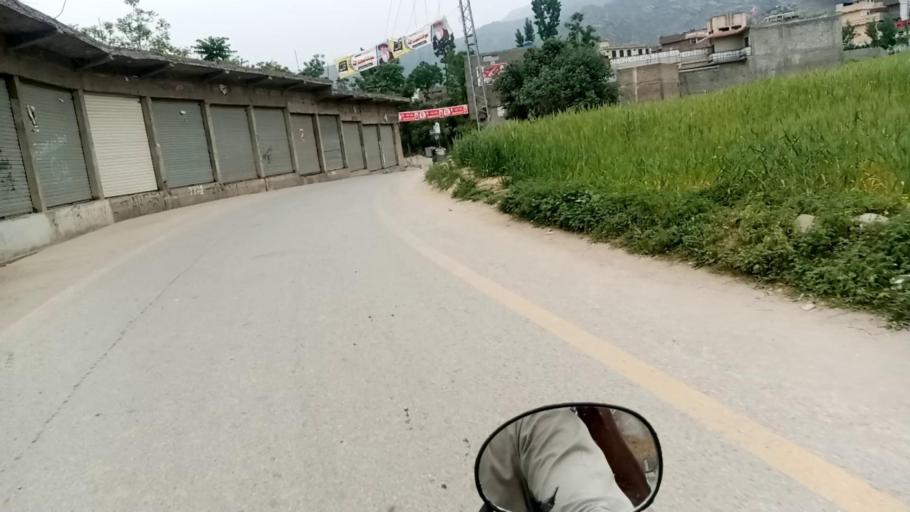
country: PK
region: Khyber Pakhtunkhwa
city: Mingora
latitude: 34.7584
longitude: 72.3780
